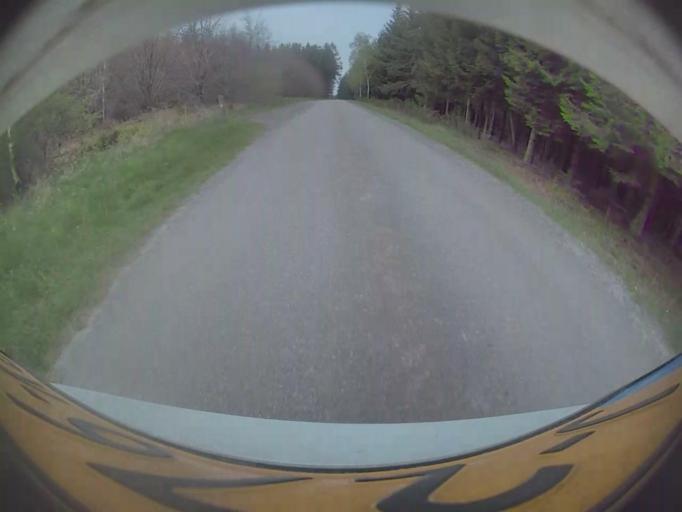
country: BE
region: Wallonia
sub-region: Province du Luxembourg
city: La Roche-en-Ardenne
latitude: 50.2335
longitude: 5.5966
